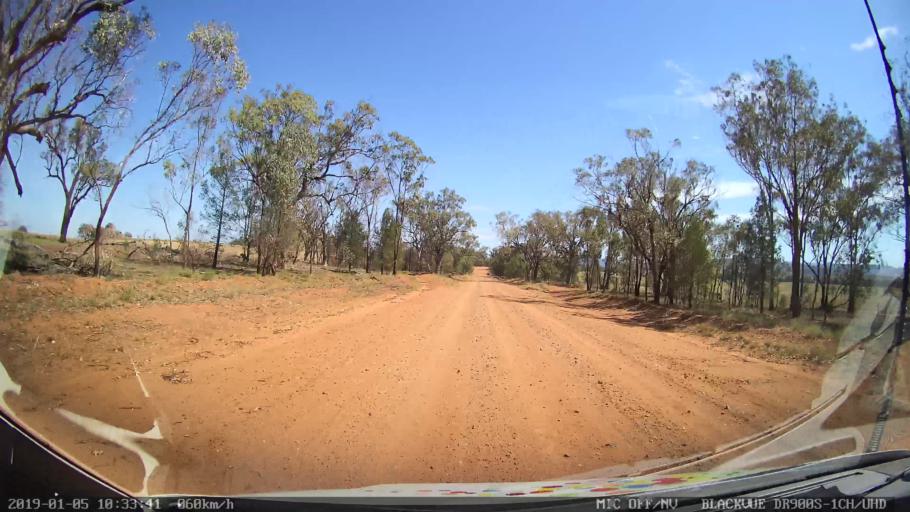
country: AU
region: New South Wales
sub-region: Gilgandra
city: Gilgandra
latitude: -31.5051
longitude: 148.9298
